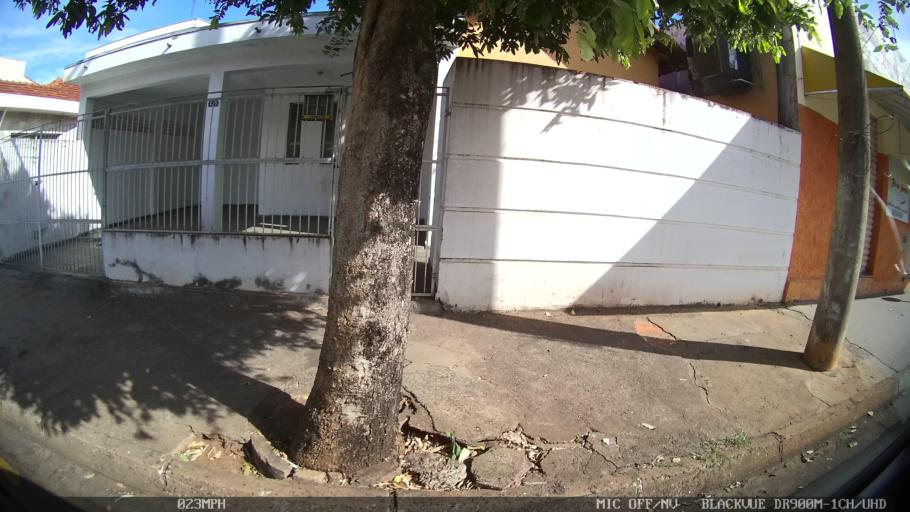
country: BR
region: Sao Paulo
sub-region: Catanduva
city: Catanduva
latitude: -21.1270
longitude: -48.9740
